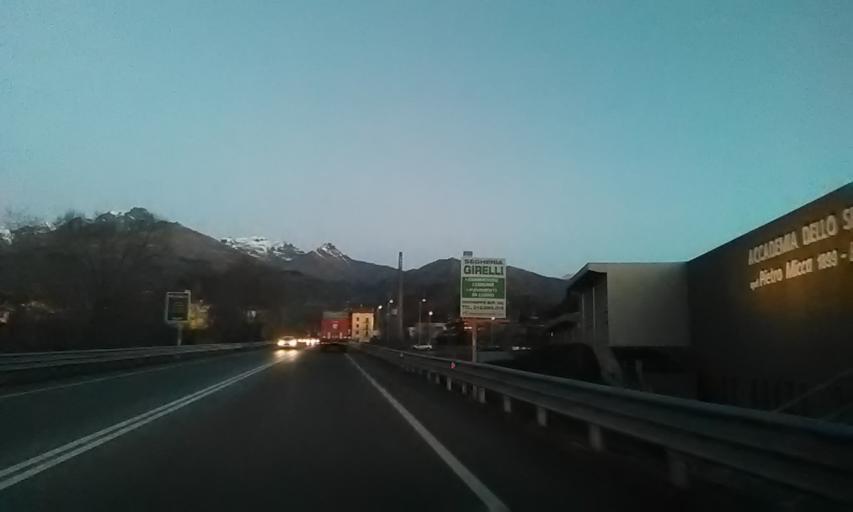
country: IT
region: Piedmont
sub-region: Provincia di Biella
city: Occhieppo Inferiore
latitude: 45.5533
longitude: 8.0307
